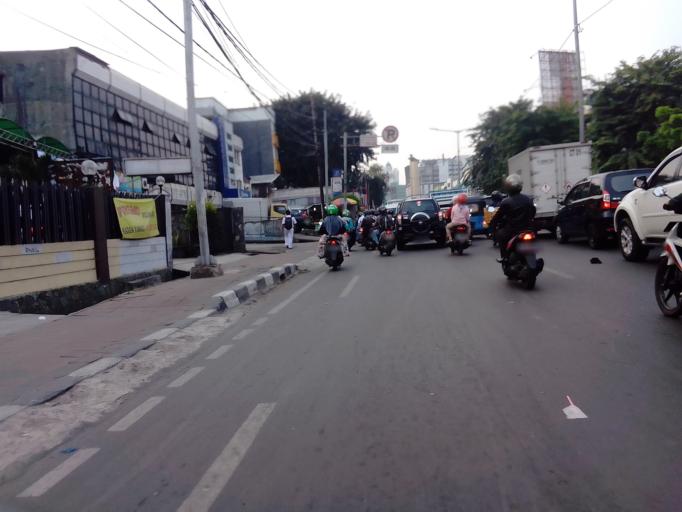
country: ID
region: Jakarta Raya
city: Jakarta
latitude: -6.1920
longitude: 106.8147
